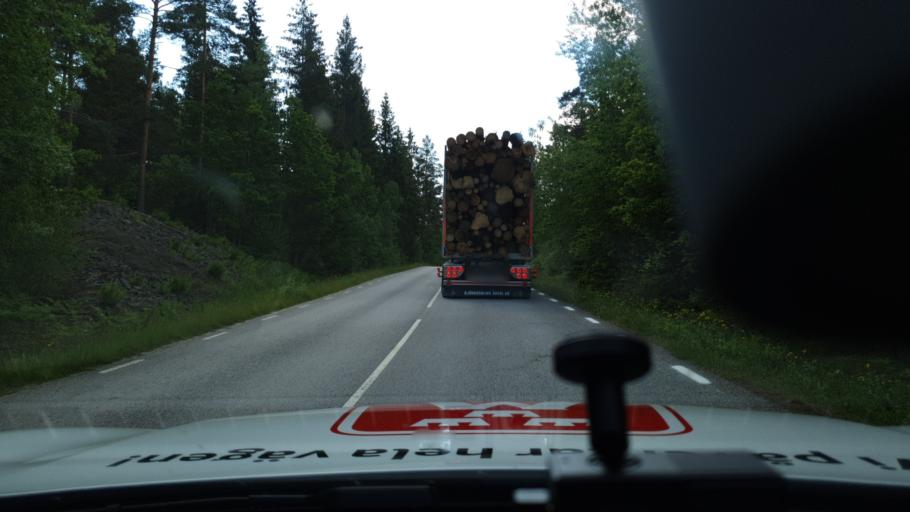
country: SE
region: Kalmar
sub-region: Vasterviks Kommun
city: Gamleby
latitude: 57.8850
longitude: 16.3193
